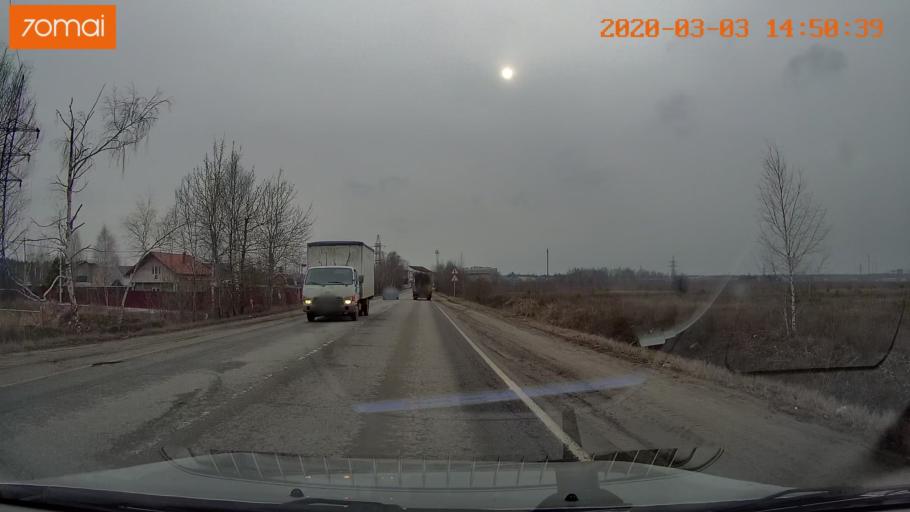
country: RU
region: Moskovskaya
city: Malakhovka
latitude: 55.6693
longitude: 38.0375
